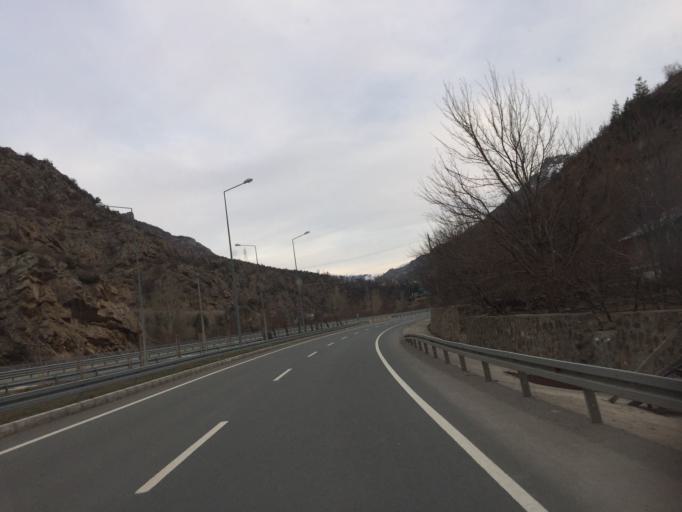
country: TR
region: Gumushane
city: Torul
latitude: 40.5475
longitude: 39.3212
